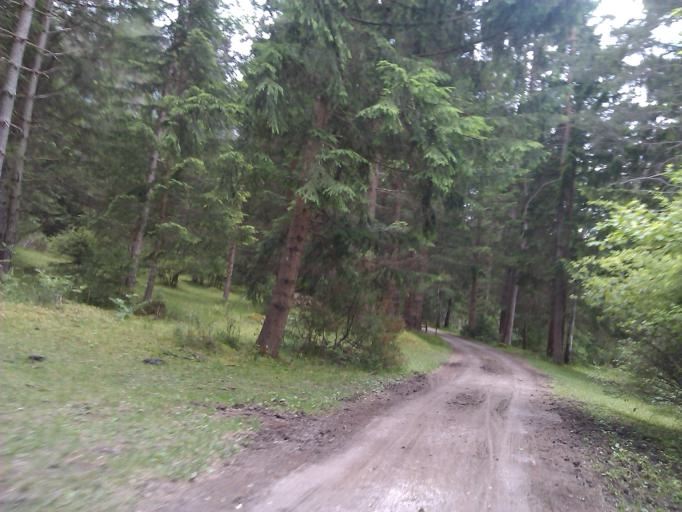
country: AT
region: Tyrol
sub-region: Politischer Bezirk Imst
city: Nassereith
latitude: 47.2852
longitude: 10.8305
